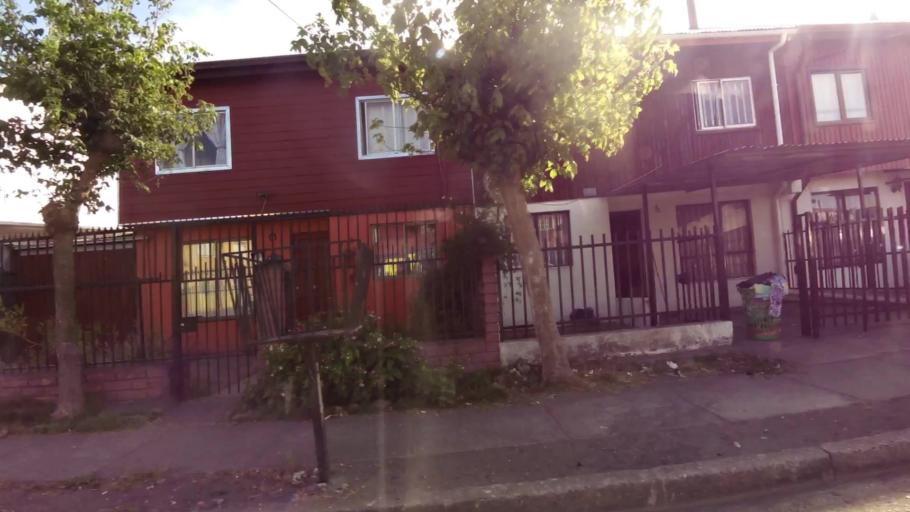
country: CL
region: Biobio
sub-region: Provincia de Concepcion
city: Concepcion
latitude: -36.7985
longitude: -73.1000
